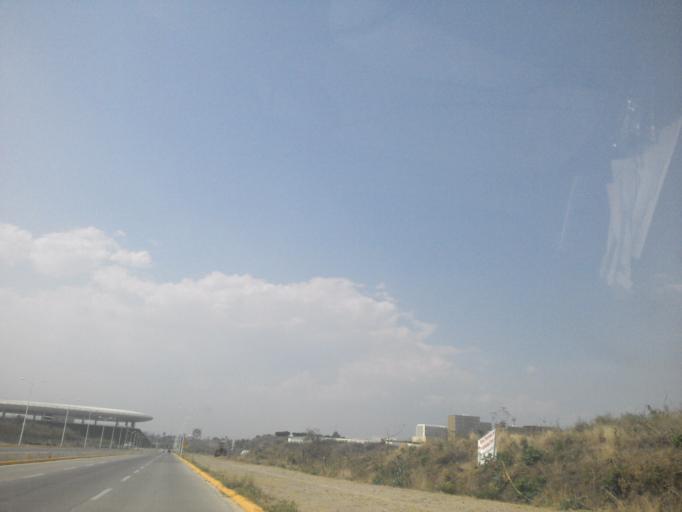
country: MX
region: Jalisco
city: Guadalajara
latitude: 20.6738
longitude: -103.4619
